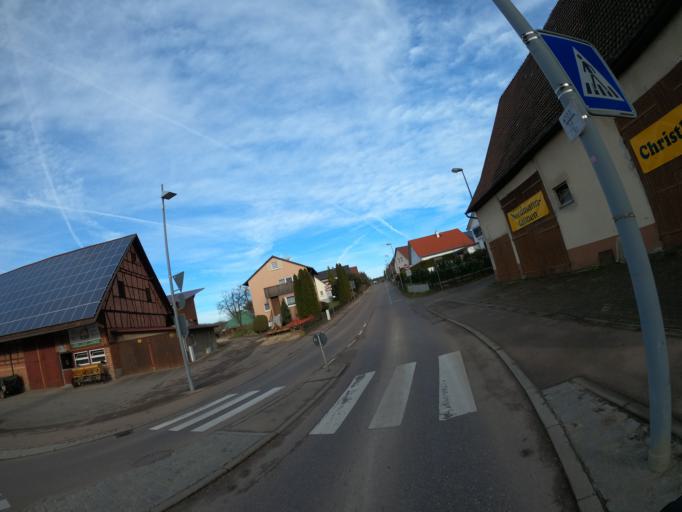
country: DE
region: Baden-Wuerttemberg
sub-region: Regierungsbezirk Stuttgart
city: Salach
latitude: 48.7071
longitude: 9.7345
